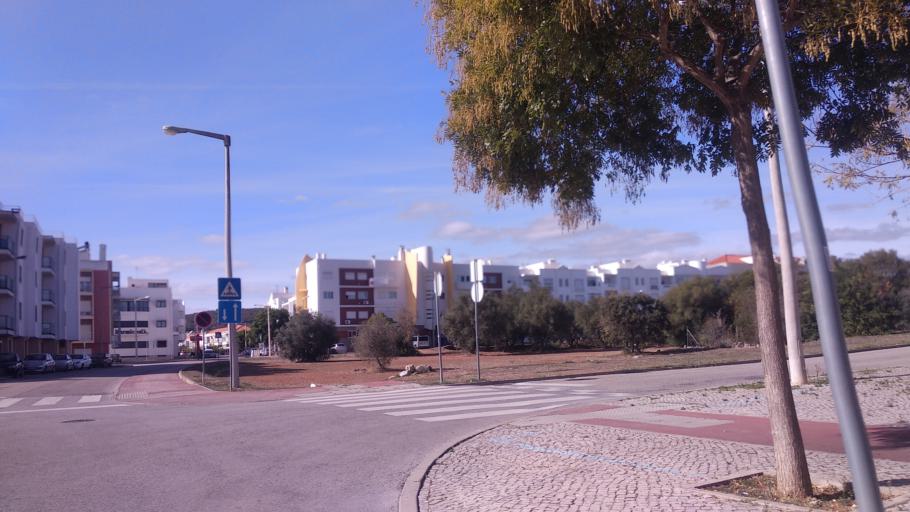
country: PT
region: Faro
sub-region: Sao Bras de Alportel
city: Sao Bras de Alportel
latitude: 37.1568
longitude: -7.8872
